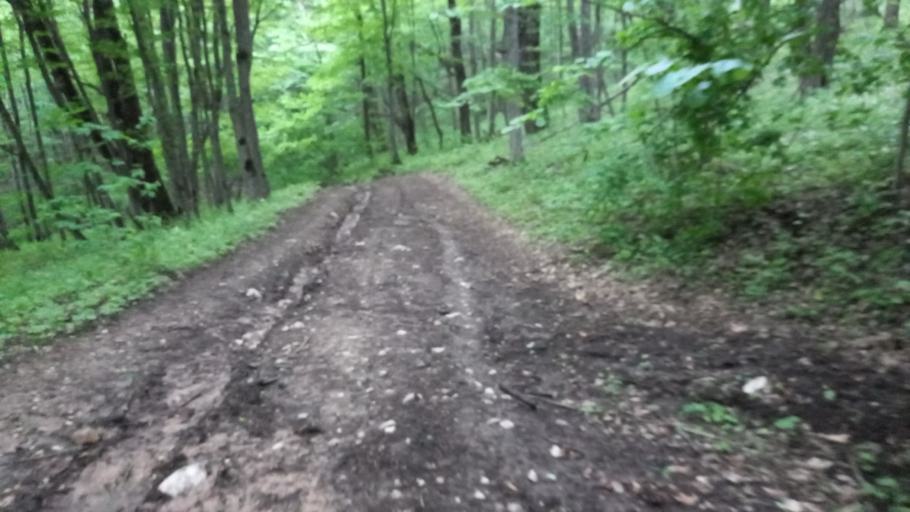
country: RU
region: Adygeya
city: Kamennomostskiy
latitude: 44.2180
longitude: 39.9938
